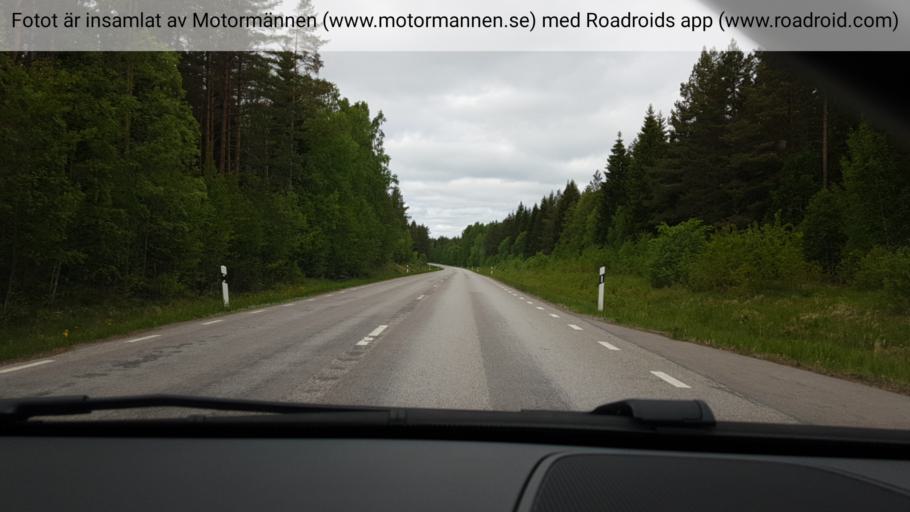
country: SE
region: Uppsala
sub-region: Heby Kommun
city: OEstervala
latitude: 60.3732
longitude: 17.2706
